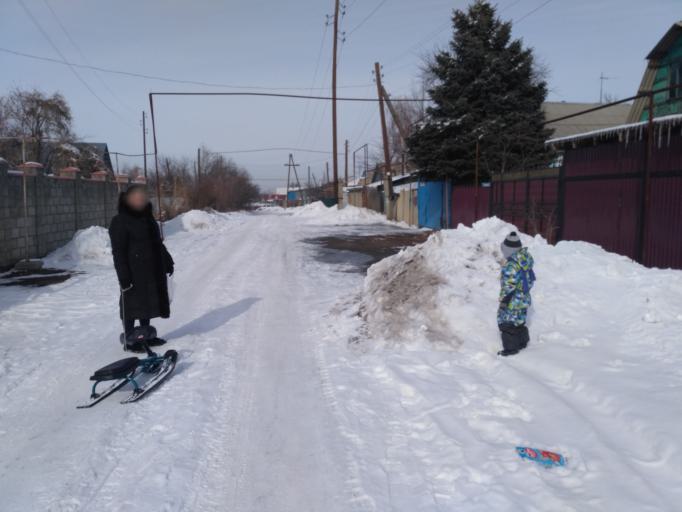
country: KZ
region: Almaty Oblysy
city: Burunday
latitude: 43.1579
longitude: 76.4022
